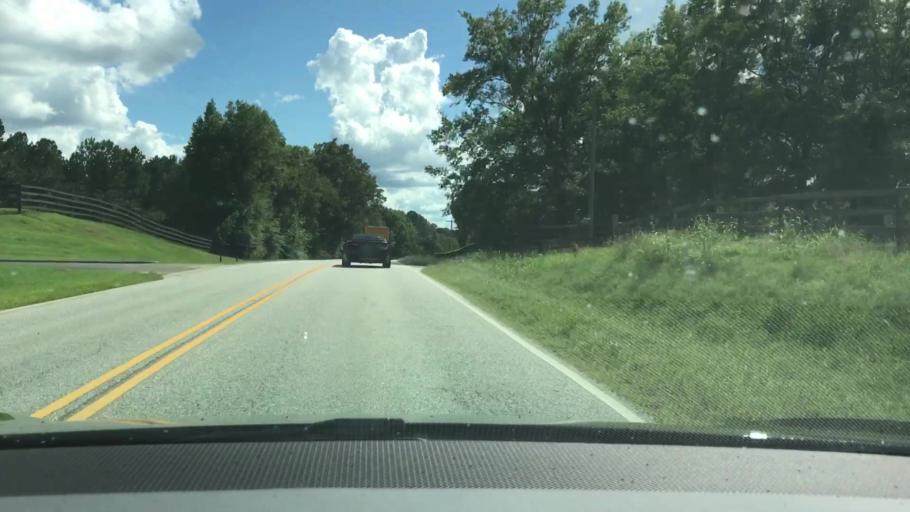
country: US
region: Alabama
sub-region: Montgomery County
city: Pike Road
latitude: 32.2128
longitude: -86.0922
